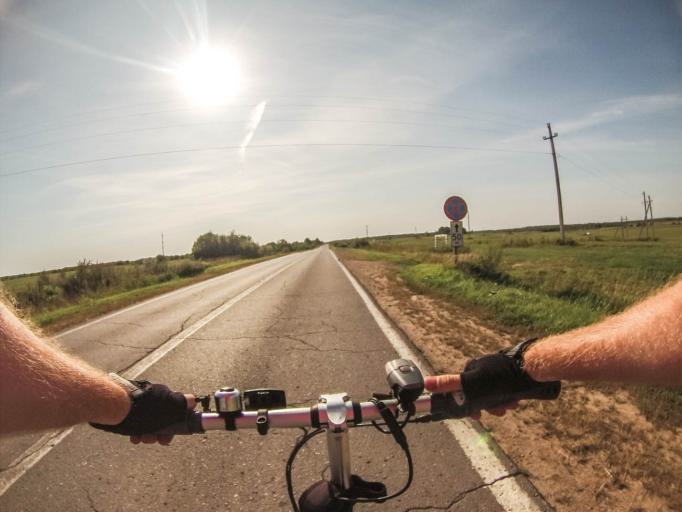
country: RU
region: Jaroslavl
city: Myshkin
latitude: 57.7746
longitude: 38.3310
